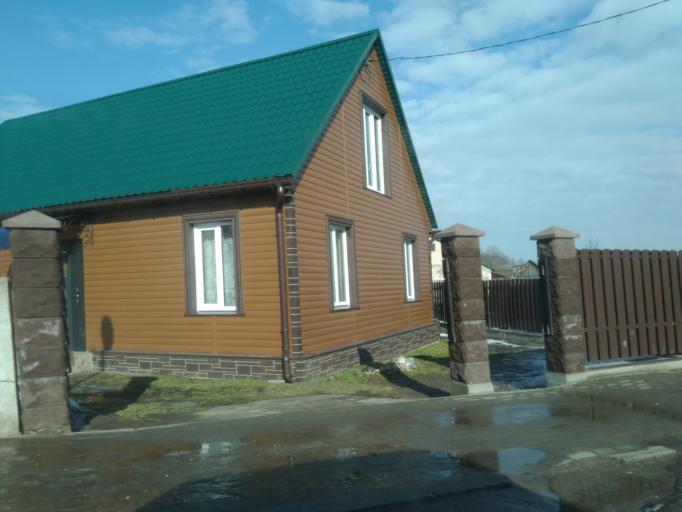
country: BY
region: Minsk
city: Nyasvizh
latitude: 53.2138
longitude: 26.6695
